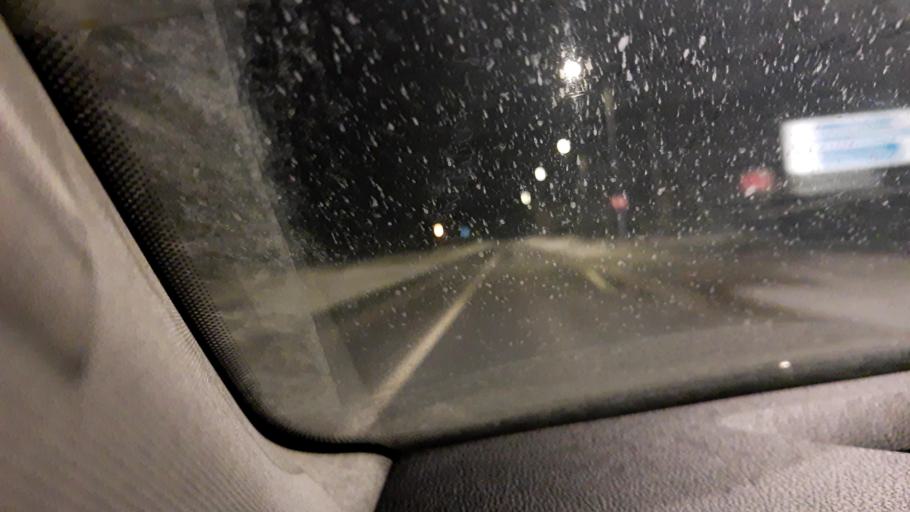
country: RU
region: Moskovskaya
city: Shemetovo
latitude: 56.6717
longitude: 38.1473
